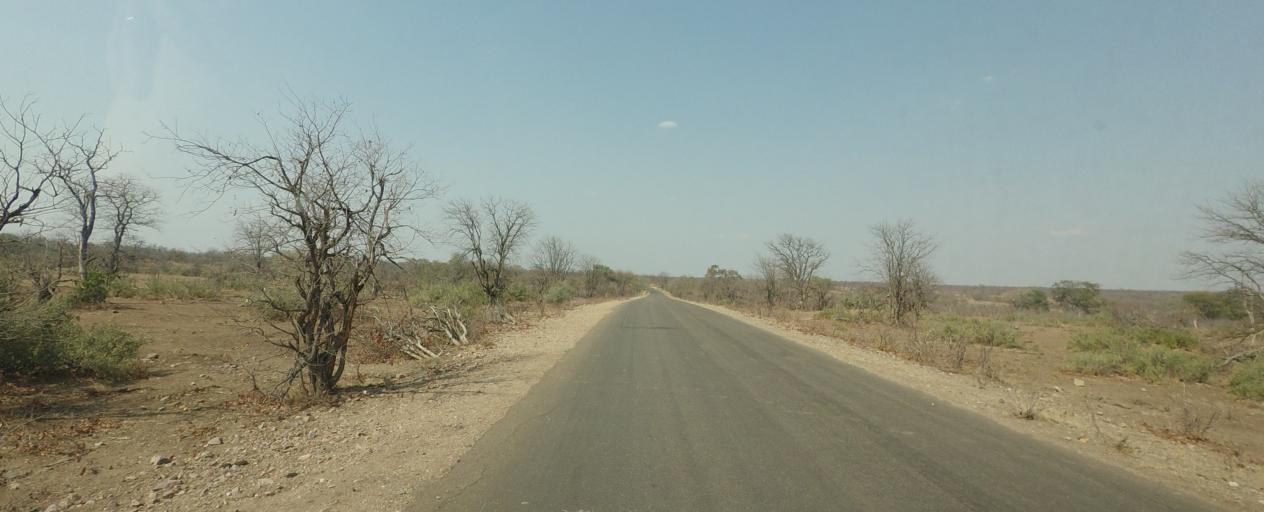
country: ZA
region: Limpopo
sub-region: Mopani District Municipality
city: Giyani
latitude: -23.1789
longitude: 31.3235
